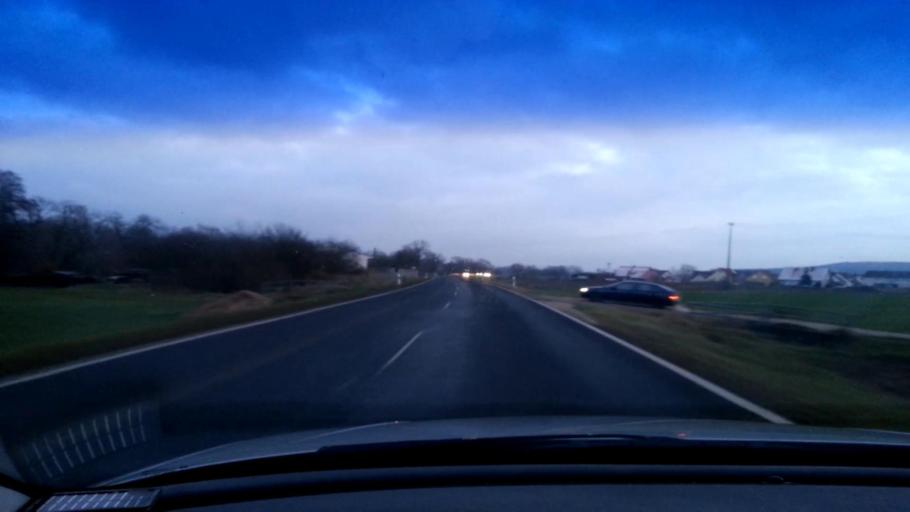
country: DE
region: Bavaria
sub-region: Upper Franconia
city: Pettstadt
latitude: 49.8362
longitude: 10.9305
